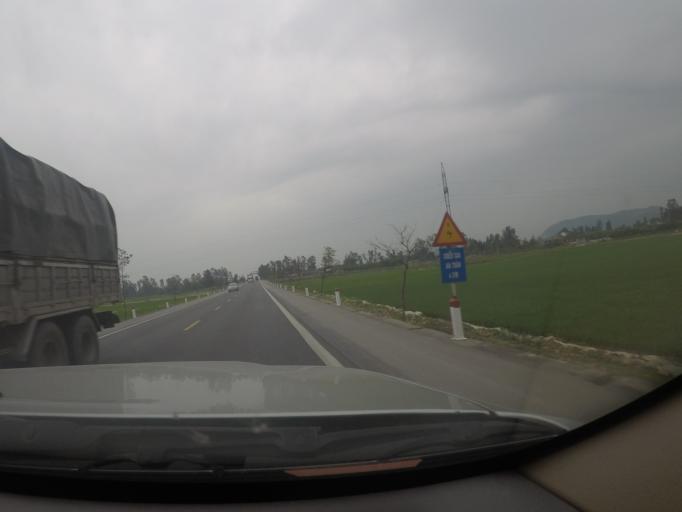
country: VN
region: Nghe An
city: Hung Nguyen
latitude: 18.7236
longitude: 105.6308
